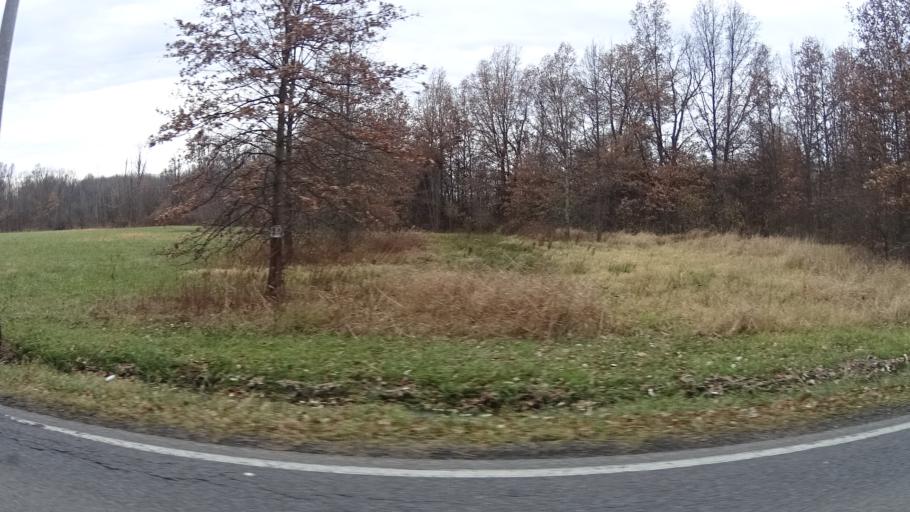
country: US
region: Ohio
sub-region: Cuyahoga County
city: Strongsville
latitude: 41.3022
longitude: -81.8778
